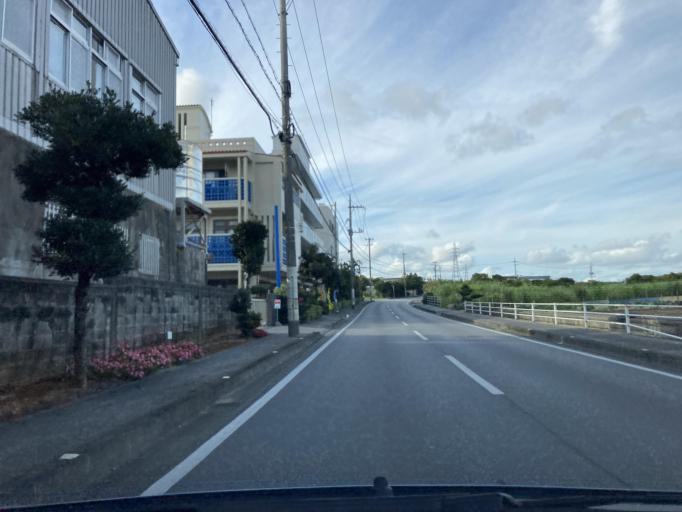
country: JP
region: Okinawa
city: Tomigusuku
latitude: 26.1531
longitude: 127.7422
